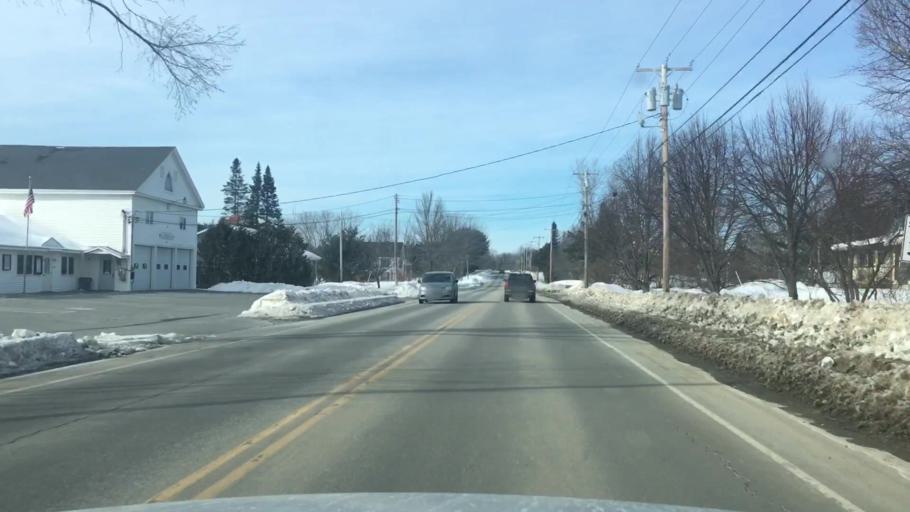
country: US
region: Maine
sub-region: Penobscot County
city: Kenduskeag
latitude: 44.9221
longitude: -68.9321
